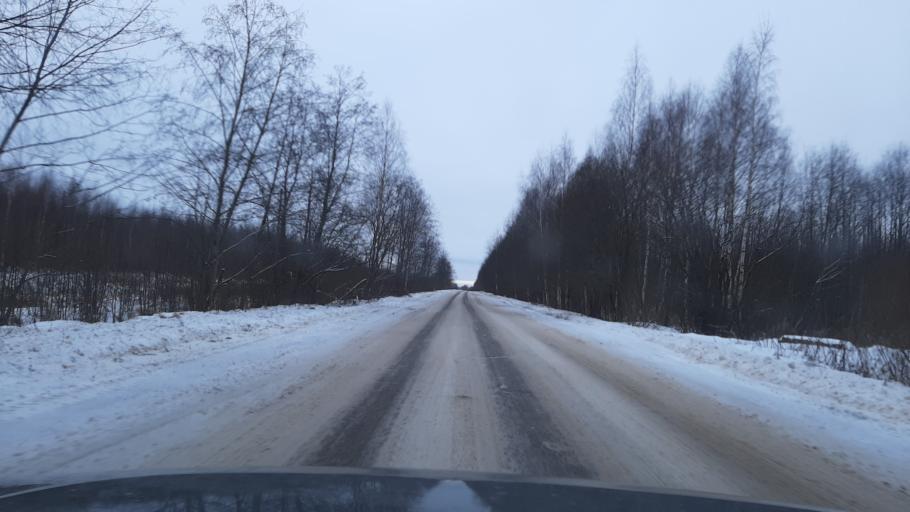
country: RU
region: Kostroma
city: Volgorechensk
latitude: 57.4415
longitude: 41.1229
